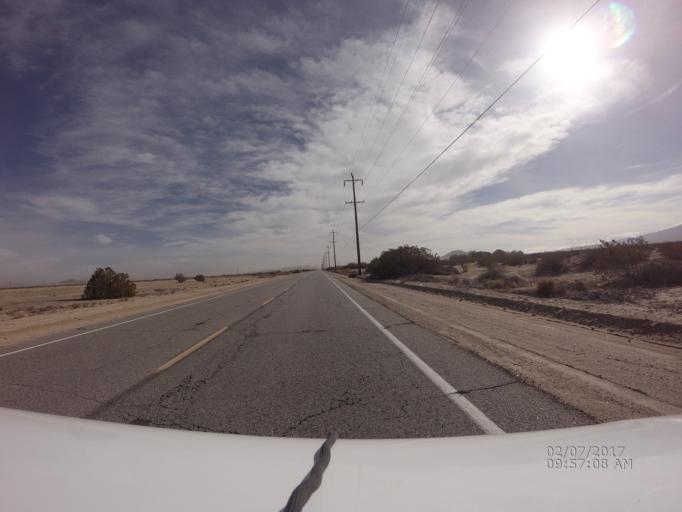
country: US
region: California
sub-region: Los Angeles County
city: Lake Los Angeles
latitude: 34.5800
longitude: -117.7779
